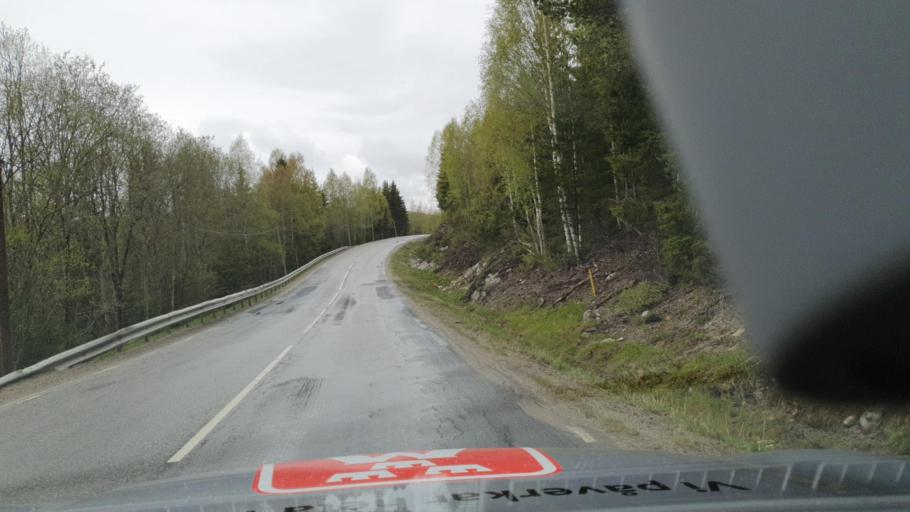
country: SE
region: Vaesternorrland
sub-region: OErnskoeldsviks Kommun
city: Bredbyn
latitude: 63.5121
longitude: 17.7529
